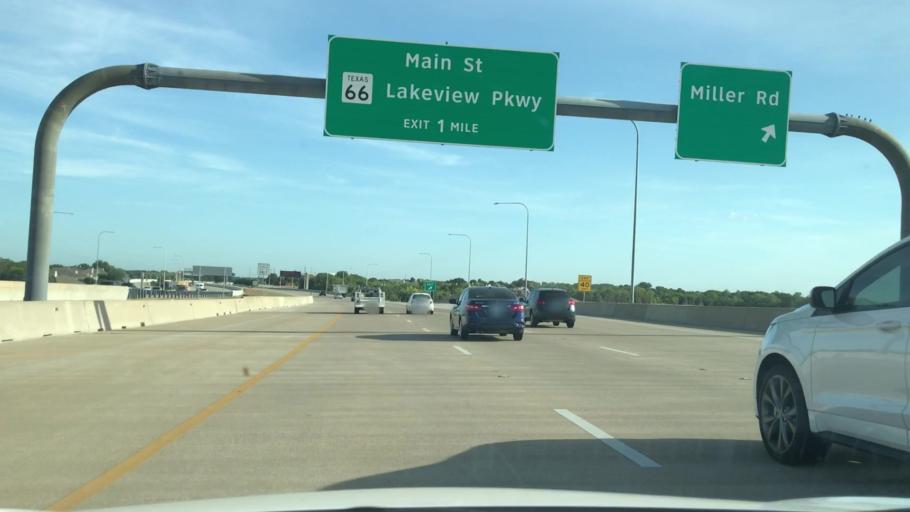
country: US
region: Texas
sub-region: Dallas County
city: Rowlett
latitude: 32.8757
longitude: -96.5526
